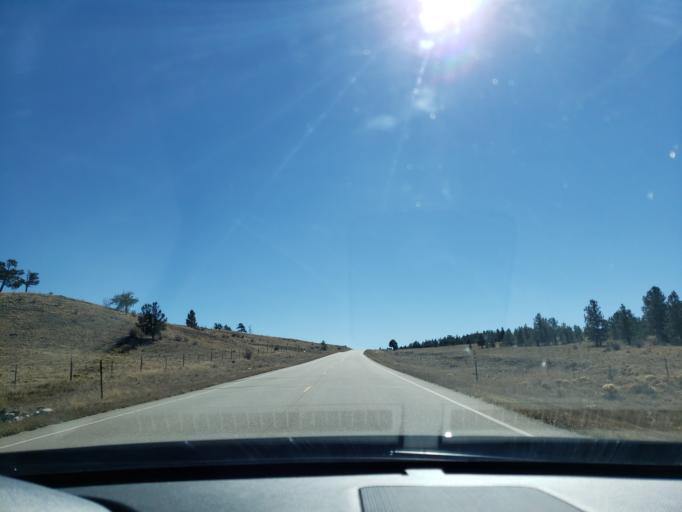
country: US
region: Colorado
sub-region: Park County
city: Fairplay
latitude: 38.9137
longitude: -105.7036
